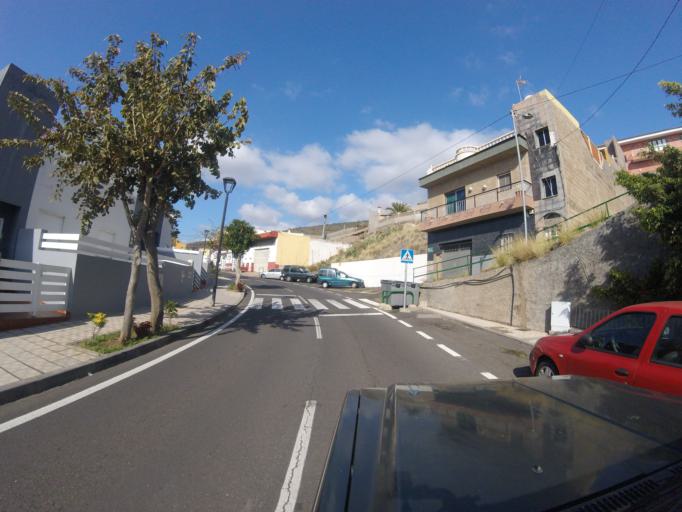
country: ES
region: Canary Islands
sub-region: Provincia de Santa Cruz de Tenerife
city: Candelaria
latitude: 28.3805
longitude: -16.3703
